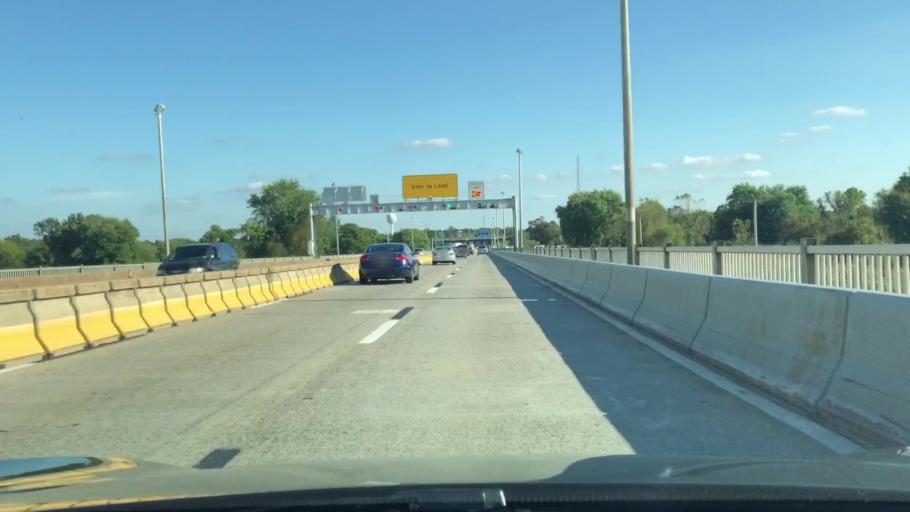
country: US
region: Pennsylvania
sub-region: Delaware County
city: Chester
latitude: 39.8142
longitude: -75.3568
